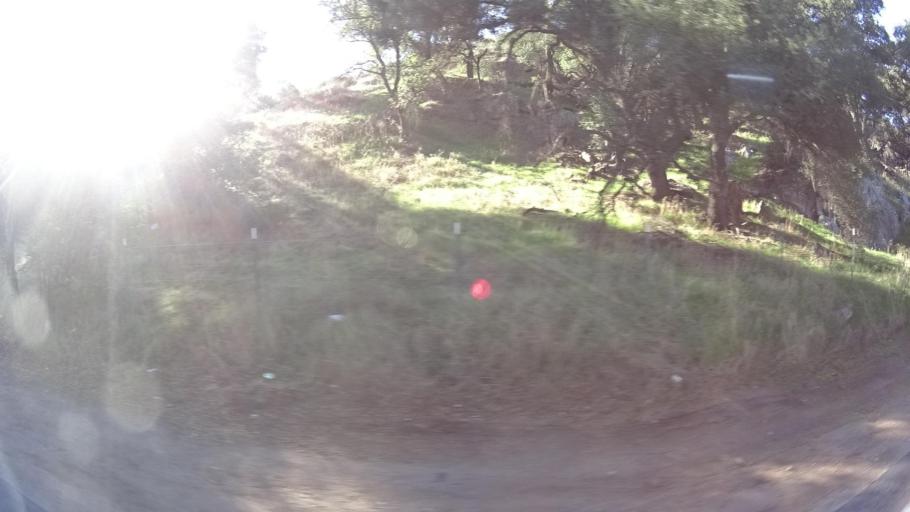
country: US
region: California
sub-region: San Diego County
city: Jamul
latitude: 32.6664
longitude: -116.8340
